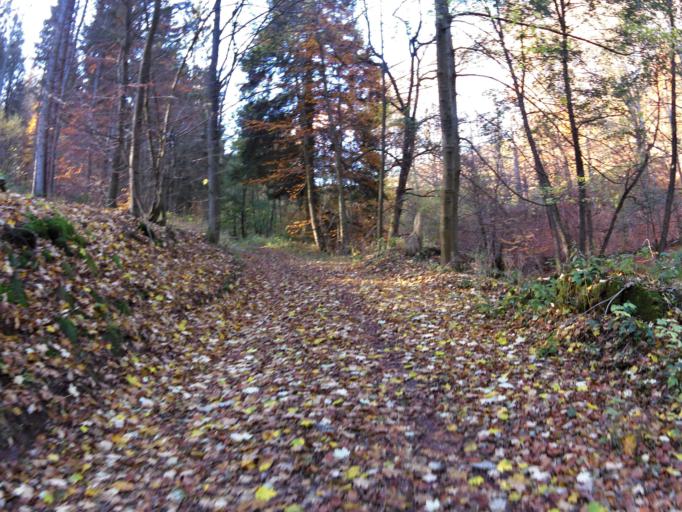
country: DE
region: Thuringia
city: Ruhla
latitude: 50.9010
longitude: 10.3510
